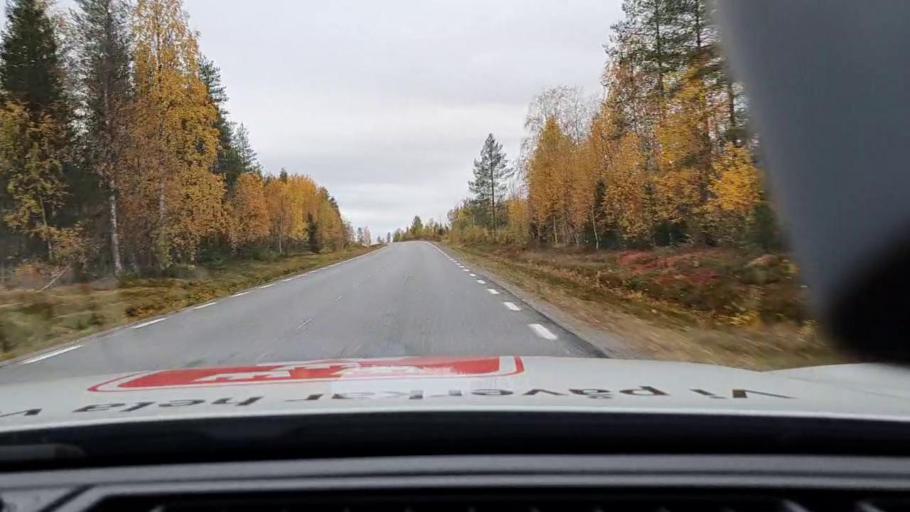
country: SE
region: Norrbotten
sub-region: Lulea Kommun
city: Ranea
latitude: 66.0511
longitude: 22.4127
